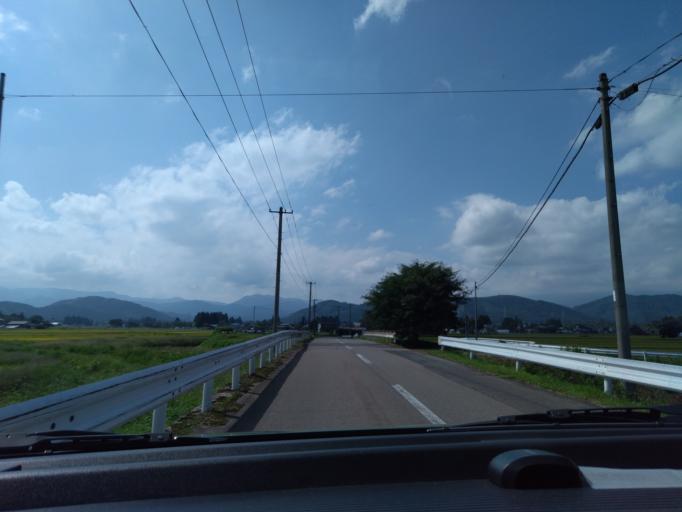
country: JP
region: Iwate
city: Shizukuishi
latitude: 39.6855
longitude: 140.9510
